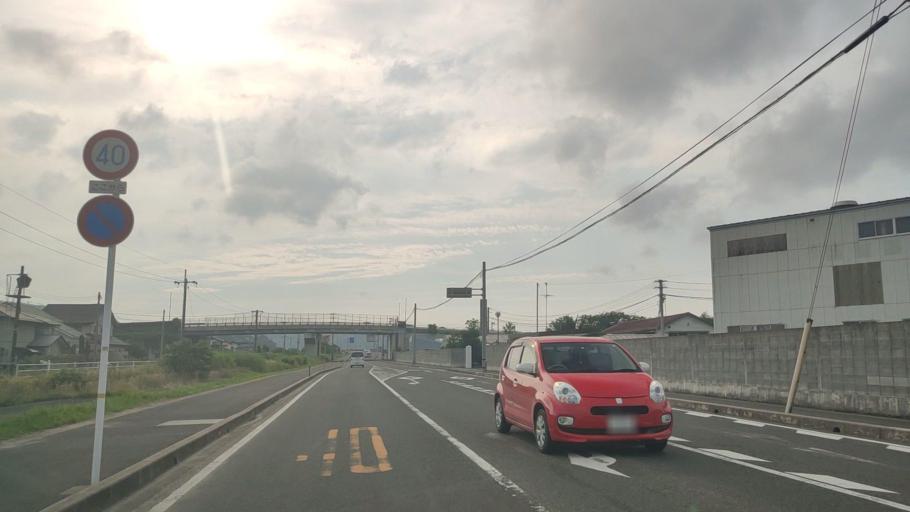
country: JP
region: Tottori
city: Kurayoshi
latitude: 35.4561
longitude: 133.8467
